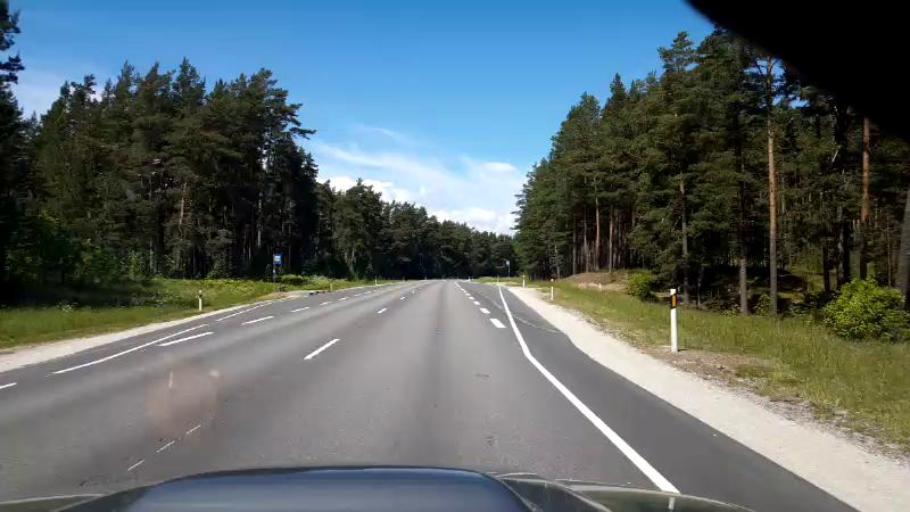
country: EE
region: Paernumaa
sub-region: Paernu linn
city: Parnu
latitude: 58.1488
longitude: 24.5007
